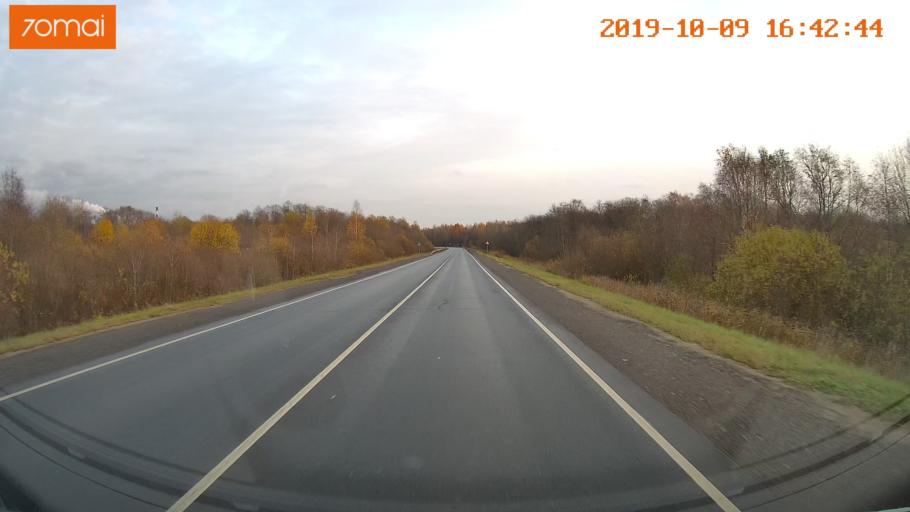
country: RU
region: Kostroma
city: Volgorechensk
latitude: 57.4591
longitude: 41.1064
